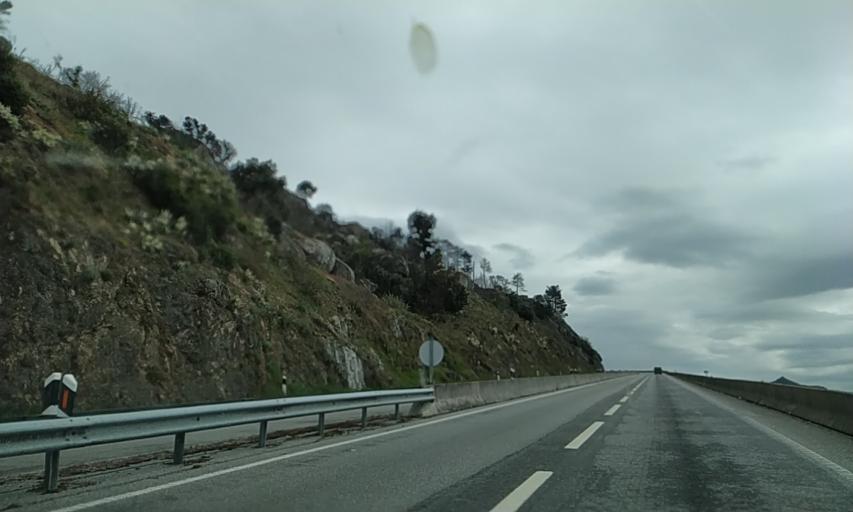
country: PT
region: Guarda
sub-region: Guarda
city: Guarda
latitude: 40.5992
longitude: -7.2754
